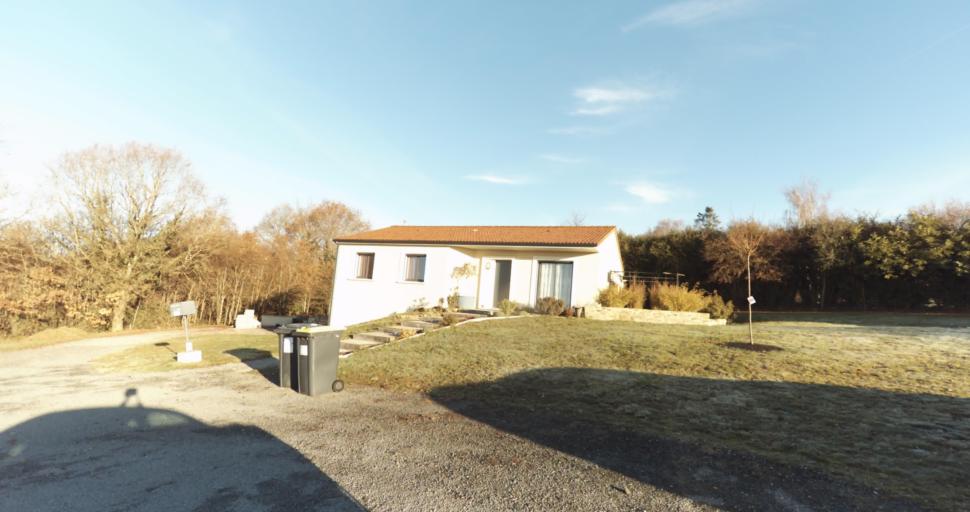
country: FR
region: Limousin
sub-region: Departement de la Haute-Vienne
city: Aixe-sur-Vienne
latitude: 45.8128
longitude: 1.1480
